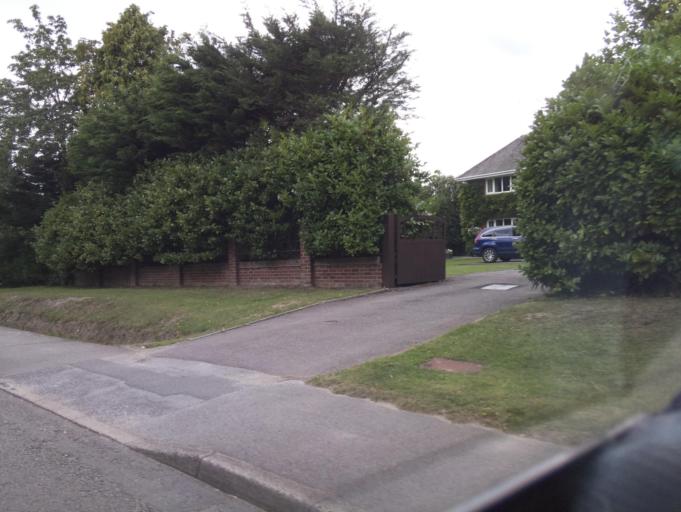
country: GB
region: England
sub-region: Hampshire
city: Lymington
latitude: 50.7484
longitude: -1.5589
